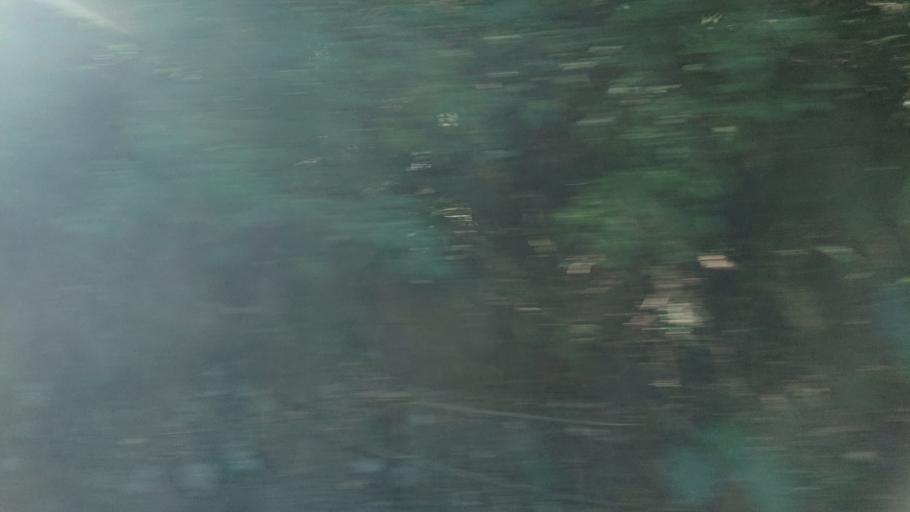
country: TW
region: Taiwan
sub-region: Chiayi
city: Jiayi Shi
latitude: 23.5359
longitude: 120.6357
